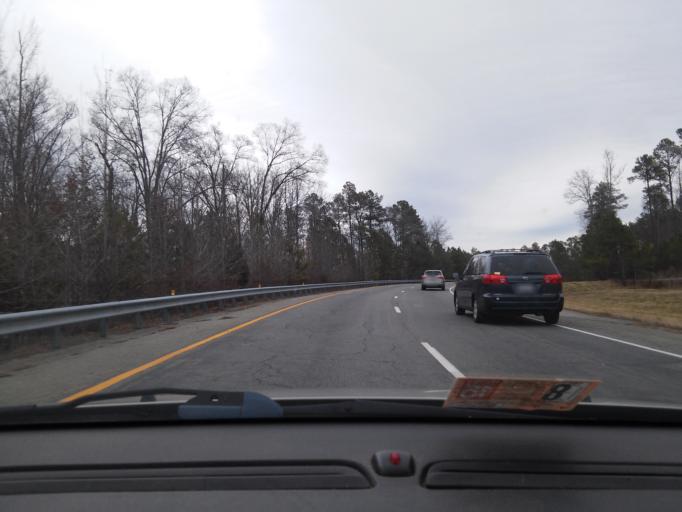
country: US
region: Virginia
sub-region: Henrico County
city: Short Pump
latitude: 37.6611
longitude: -77.6581
